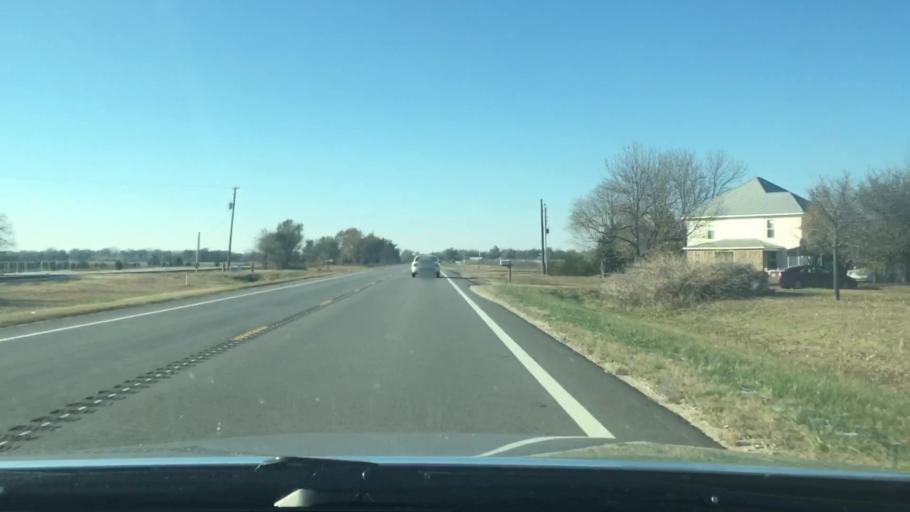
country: US
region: Kansas
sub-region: Reno County
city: Nickerson
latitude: 38.1367
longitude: -98.0679
